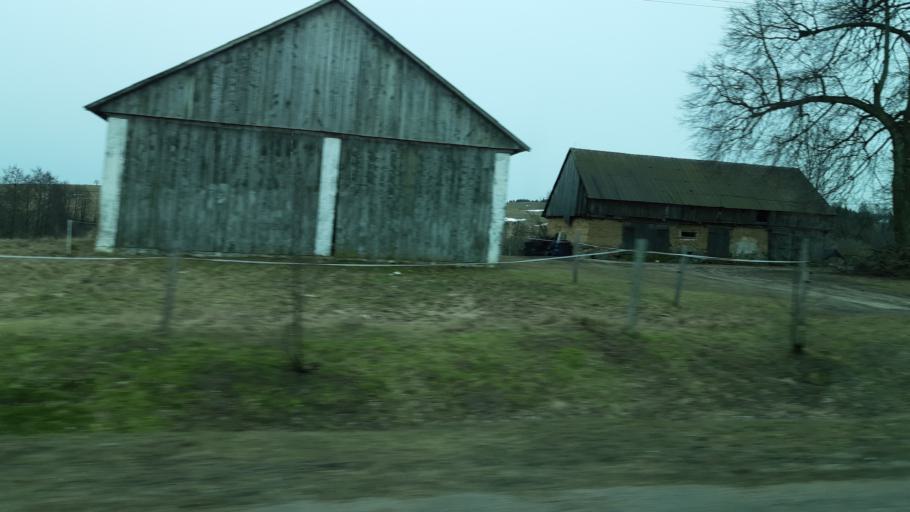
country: PL
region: Podlasie
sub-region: Suwalki
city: Suwalki
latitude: 54.3323
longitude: 22.9435
